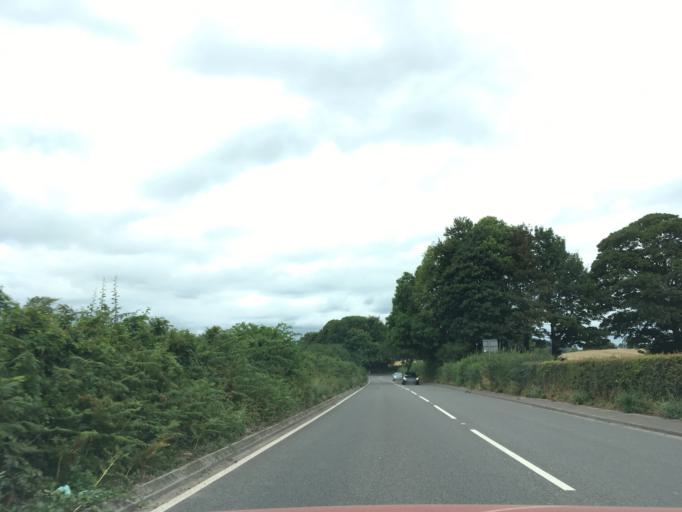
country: GB
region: Wales
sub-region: Monmouthshire
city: Abergavenny
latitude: 51.7990
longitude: -3.0067
